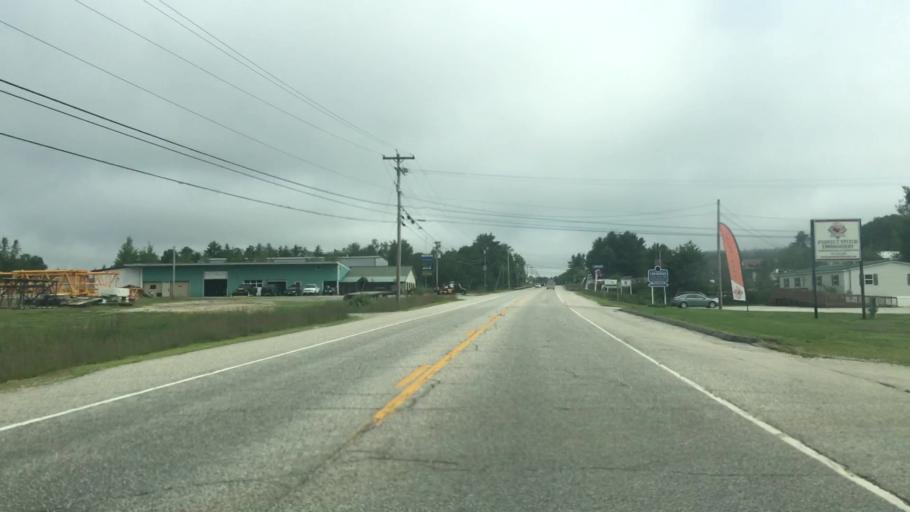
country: US
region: Maine
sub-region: Oxford County
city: South Paris
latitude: 44.2370
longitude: -70.5139
